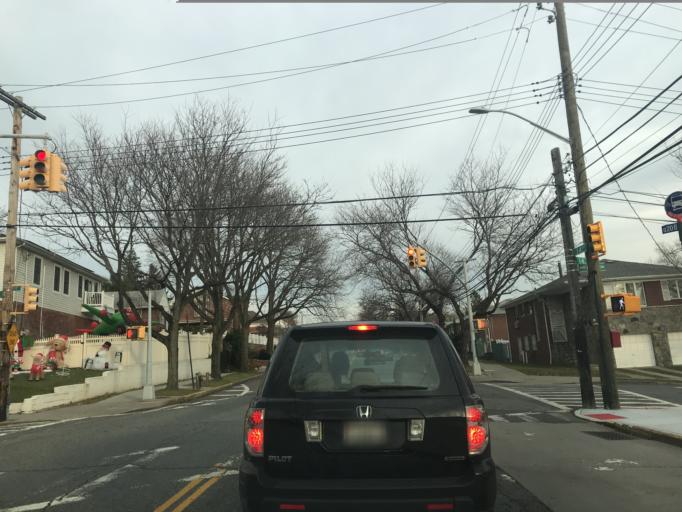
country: US
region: New York
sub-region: Bronx
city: The Bronx
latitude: 40.7866
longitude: -73.8266
